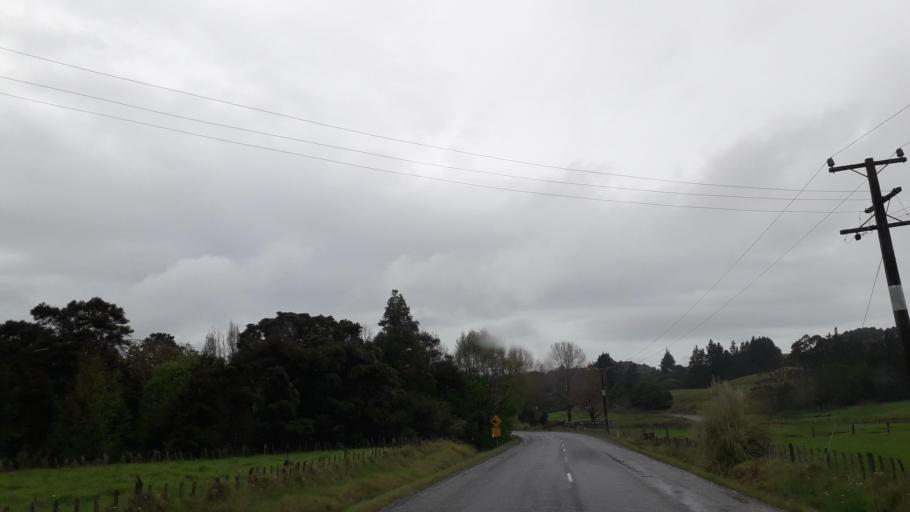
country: NZ
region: Northland
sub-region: Far North District
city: Kaitaia
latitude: -35.3613
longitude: 173.4805
